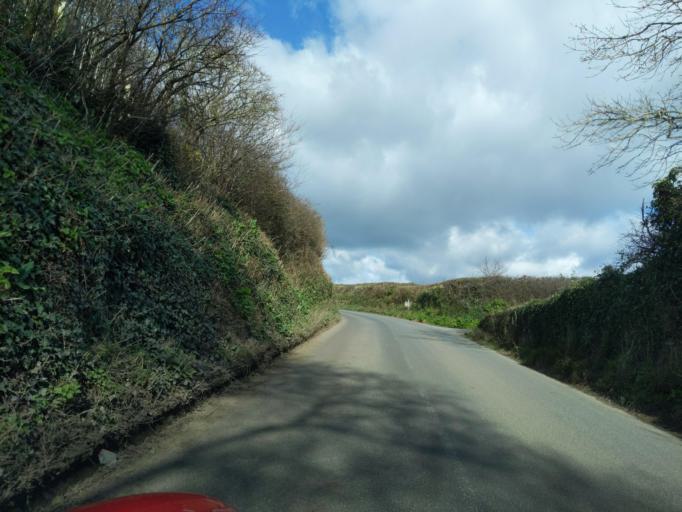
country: GB
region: England
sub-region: Devon
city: Kingsbridge
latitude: 50.2902
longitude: -3.7702
